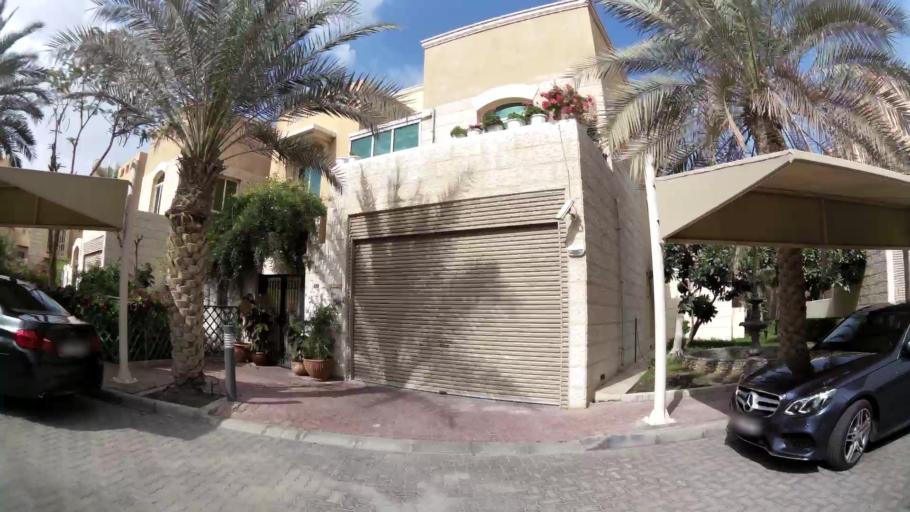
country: AE
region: Abu Dhabi
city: Abu Dhabi
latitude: 24.4440
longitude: 54.3703
